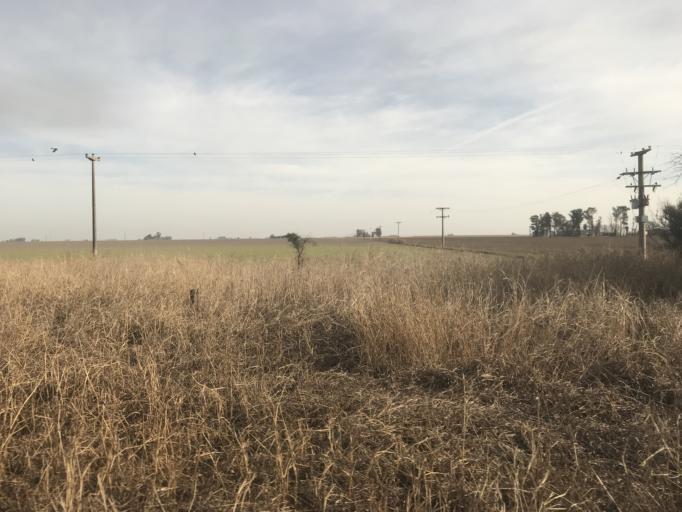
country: AR
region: Cordoba
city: Laguna Larga
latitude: -31.7521
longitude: -63.8248
